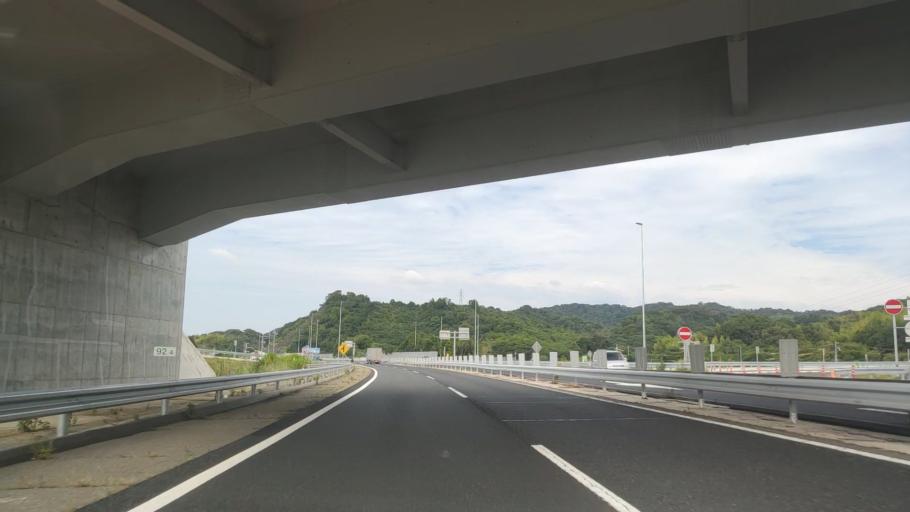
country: JP
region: Wakayama
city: Wakayama-shi
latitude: 34.2083
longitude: 135.2287
